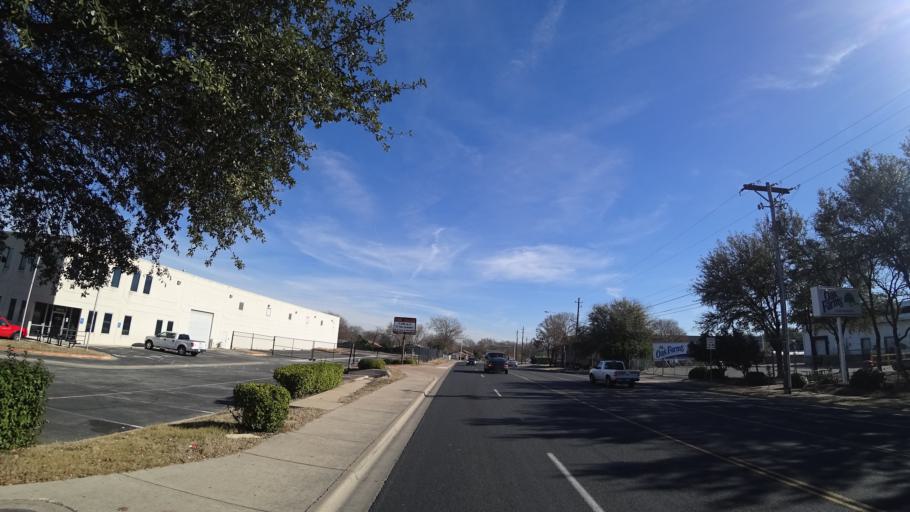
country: US
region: Texas
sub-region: Travis County
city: Wells Branch
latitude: 30.3786
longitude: -97.7116
